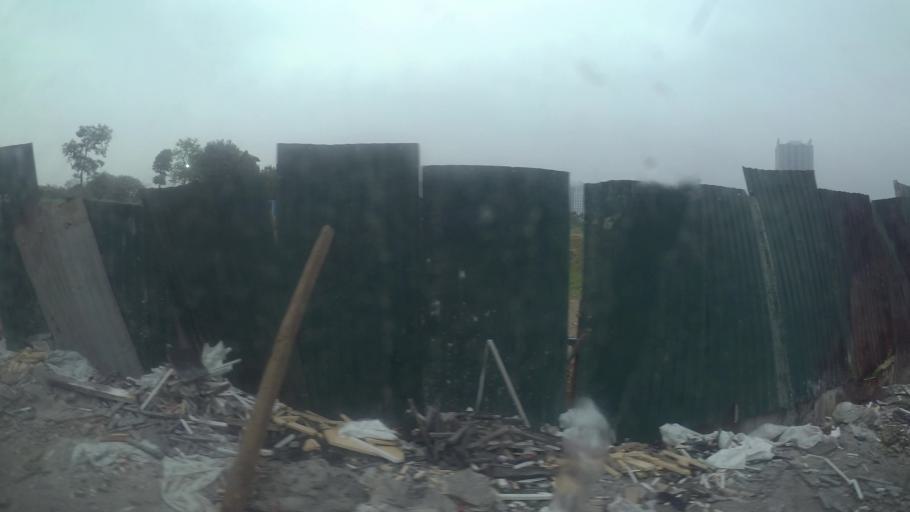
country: VN
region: Ha Noi
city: Cau Giay
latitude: 21.0217
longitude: 105.7849
